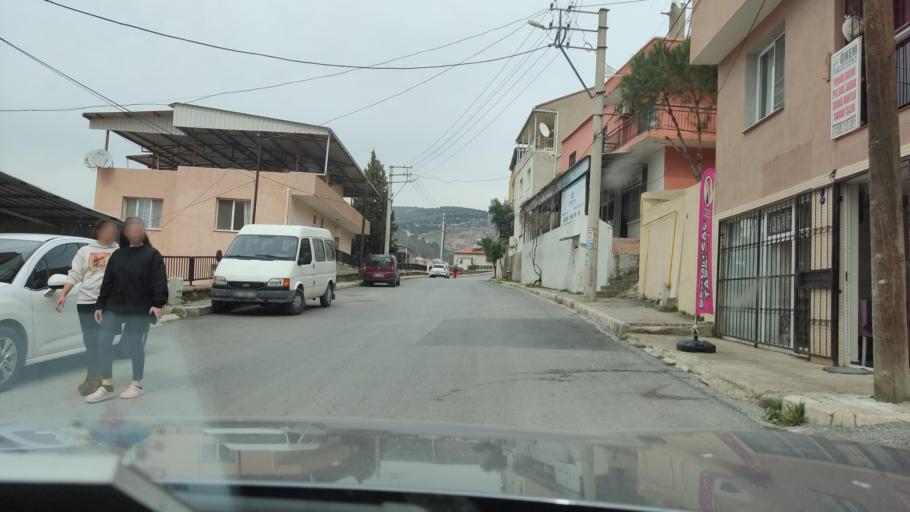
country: TR
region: Izmir
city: Karsiyaka
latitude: 38.4985
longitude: 27.0725
